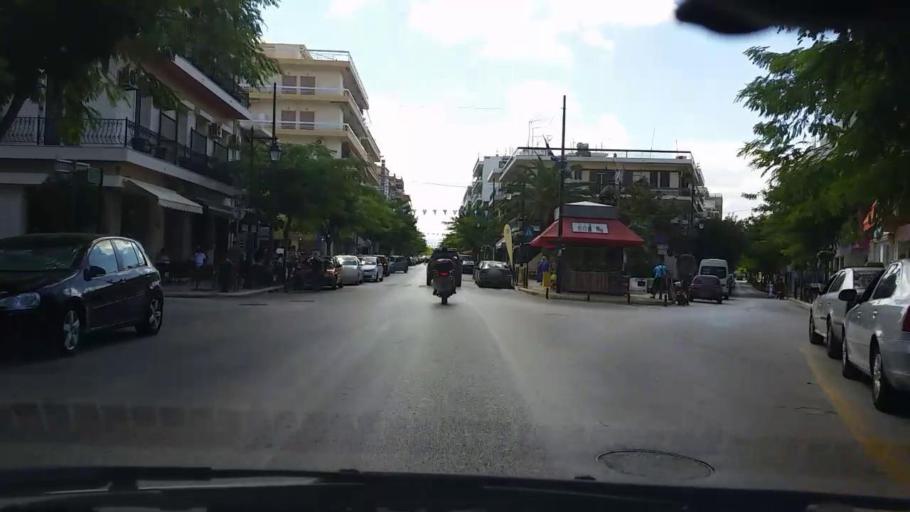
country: GR
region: Peloponnese
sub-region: Nomos Korinthias
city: Loutraki
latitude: 37.9761
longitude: 22.9774
